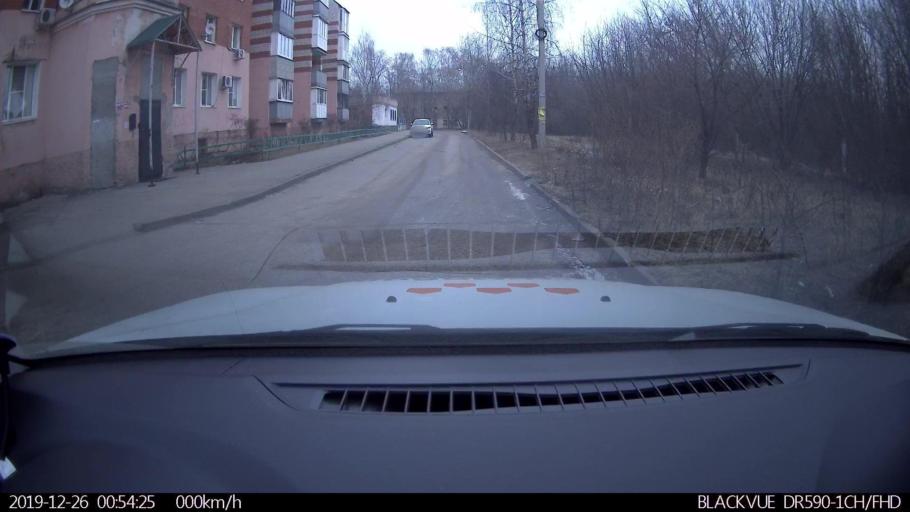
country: RU
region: Nizjnij Novgorod
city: Nizhniy Novgorod
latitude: 56.3010
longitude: 43.8812
